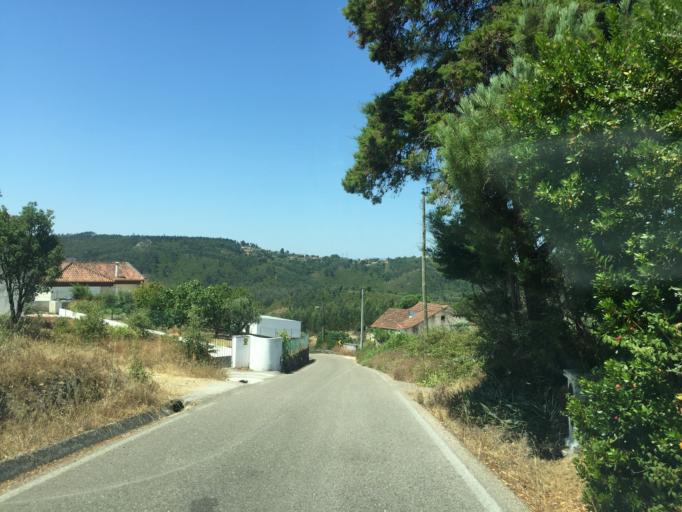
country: PT
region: Santarem
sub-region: Tomar
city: Tomar
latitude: 39.5771
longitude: -8.3000
